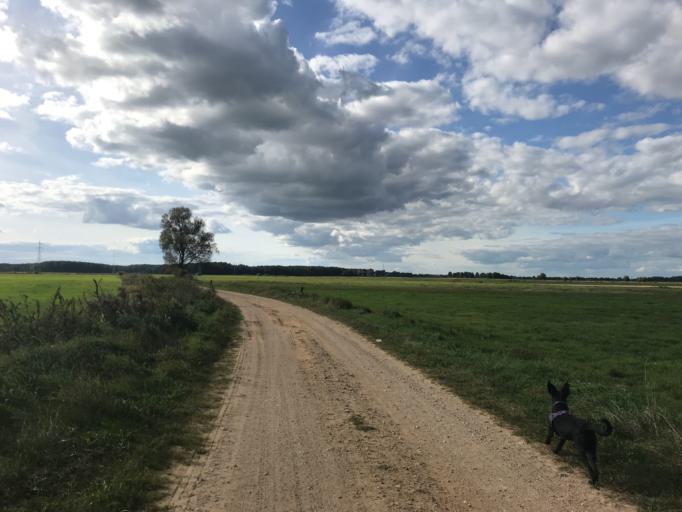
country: PL
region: Podlasie
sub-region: Powiat zambrowski
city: Rutki
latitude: 53.2021
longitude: 22.5832
